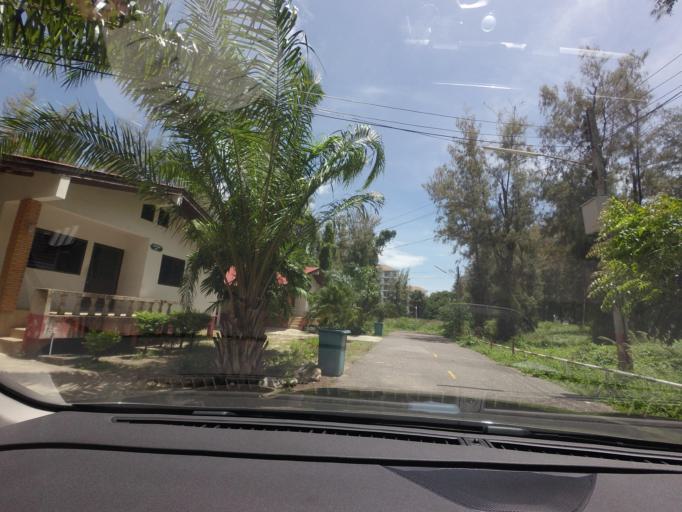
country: TH
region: Prachuap Khiri Khan
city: Hua Hin
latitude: 12.5011
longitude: 99.9741
